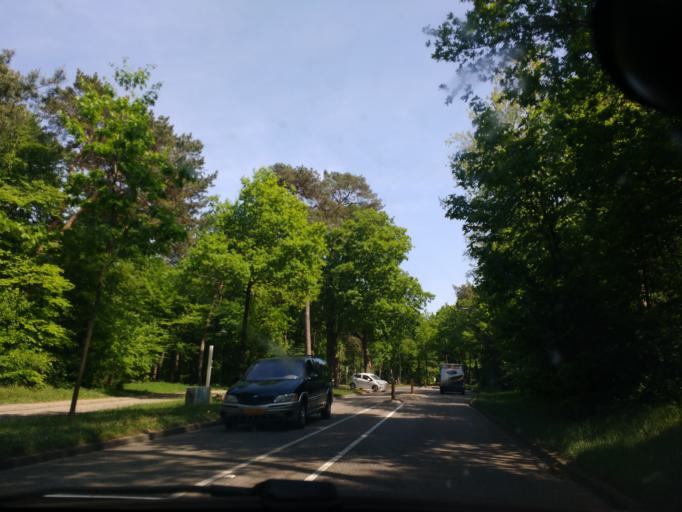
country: NL
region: Utrecht
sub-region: Gemeente Utrechtse Heuvelrug
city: Driebergen-Rijsenburg
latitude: 52.0629
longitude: 5.2804
